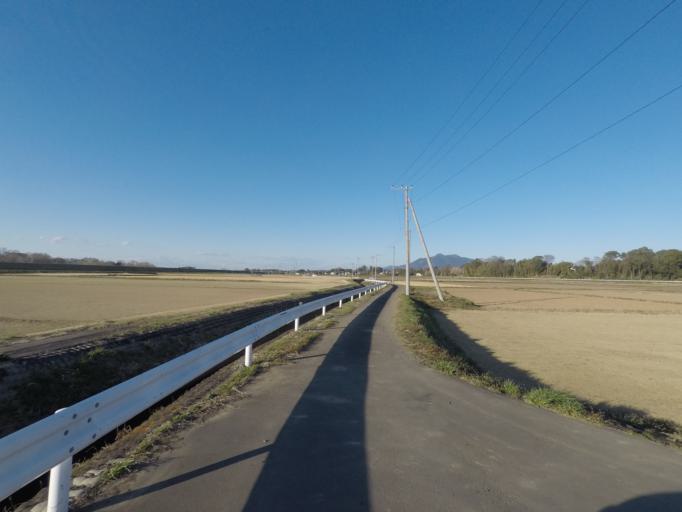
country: JP
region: Ibaraki
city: Ishige
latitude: 36.1371
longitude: 140.0025
